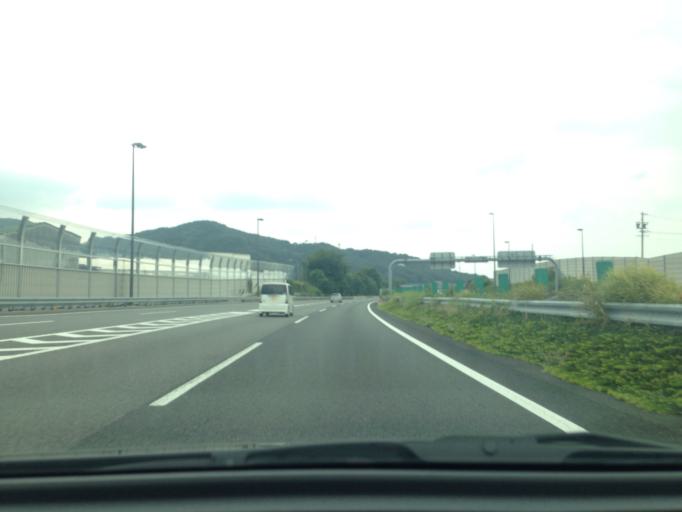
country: JP
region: Aichi
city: Shinshiro
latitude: 34.8225
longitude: 137.5489
